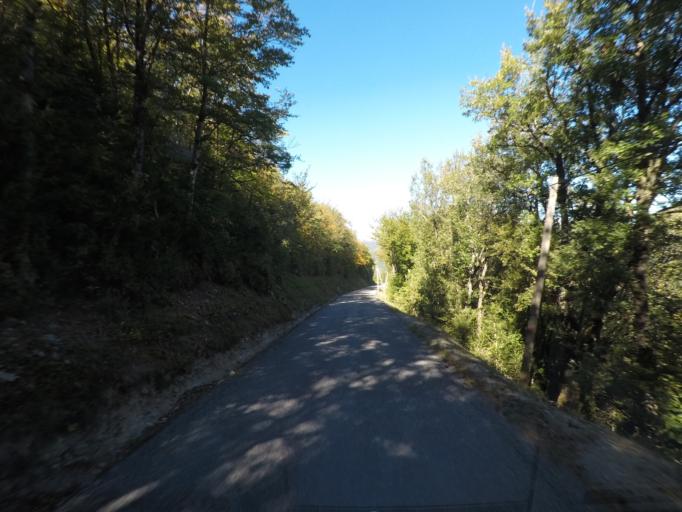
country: FR
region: Rhone-Alpes
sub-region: Departement de la Drome
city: Die
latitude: 44.5777
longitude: 5.2903
